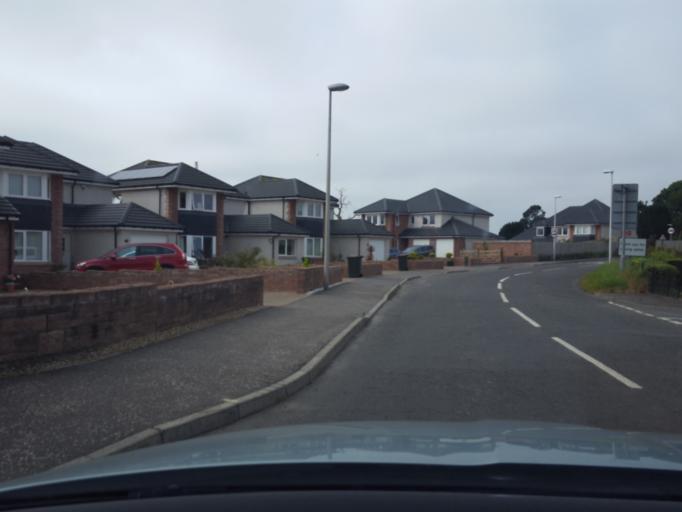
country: GB
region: Scotland
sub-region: Perth and Kinross
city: Bridge of Earn
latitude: 56.3488
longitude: -3.4099
